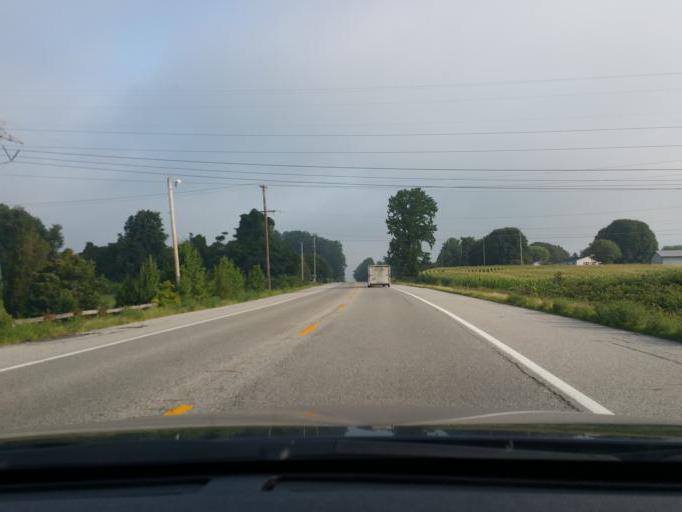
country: US
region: Maryland
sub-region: Cecil County
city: Rising Sun
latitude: 39.6790
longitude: -76.0742
